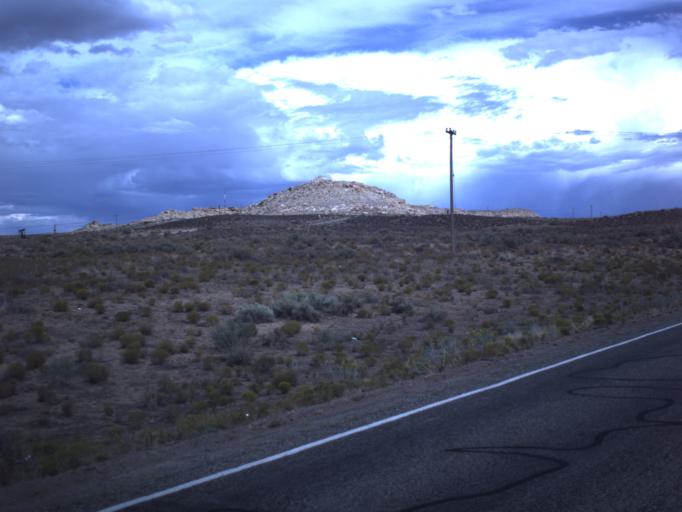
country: US
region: Utah
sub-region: San Juan County
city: Blanding
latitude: 37.2398
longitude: -109.2403
